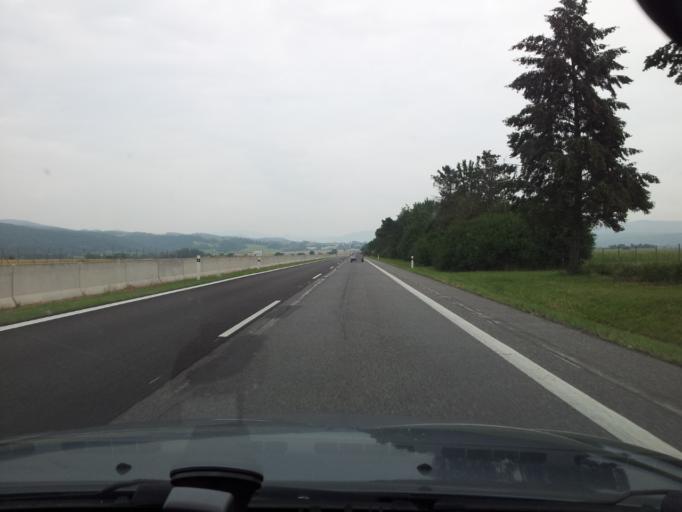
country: SK
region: Banskobystricky
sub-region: Okres Banska Bystrica
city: Zvolen
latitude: 48.6347
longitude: 19.1198
